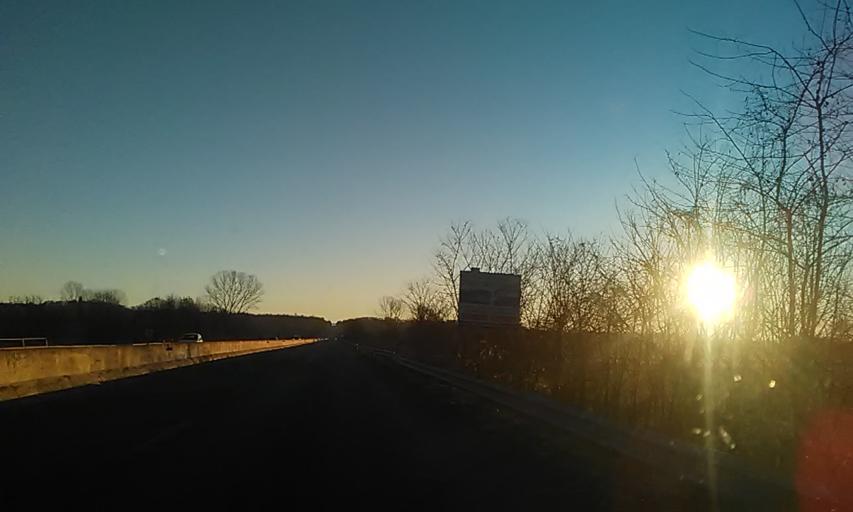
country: IT
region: Piedmont
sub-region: Provincia di Biella
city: Cossato
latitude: 45.5528
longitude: 8.1855
